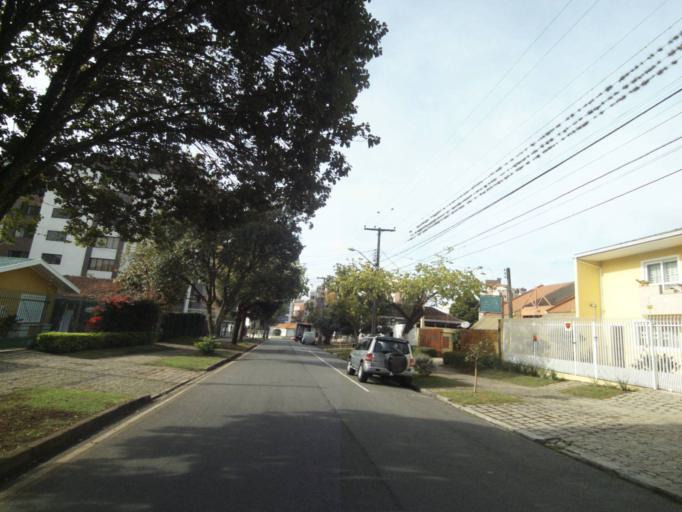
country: BR
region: Parana
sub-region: Curitiba
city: Curitiba
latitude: -25.4188
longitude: -49.2570
